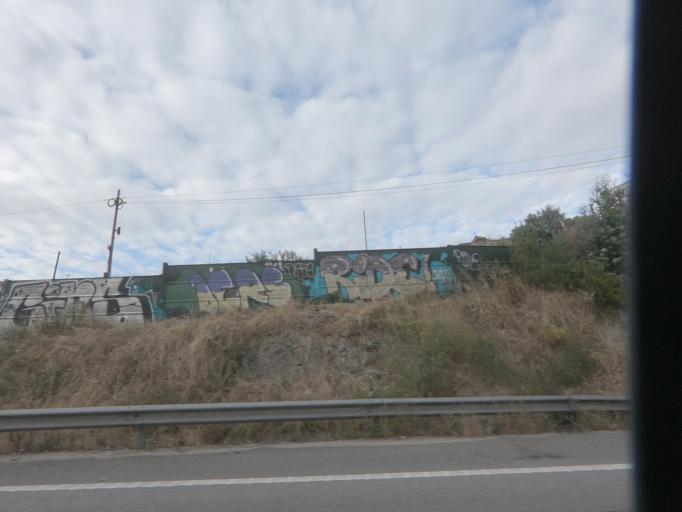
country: PT
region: Porto
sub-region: Matosinhos
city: Leca da Palmeira
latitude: 41.1987
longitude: -8.6861
